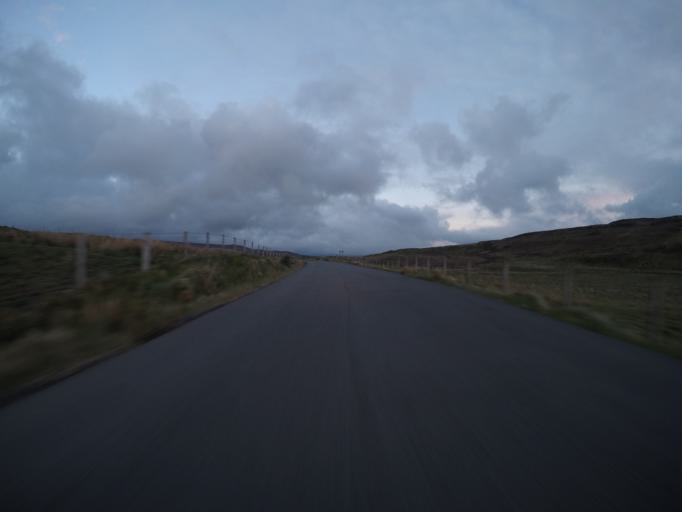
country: GB
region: Scotland
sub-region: Highland
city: Portree
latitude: 57.5978
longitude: -6.3757
